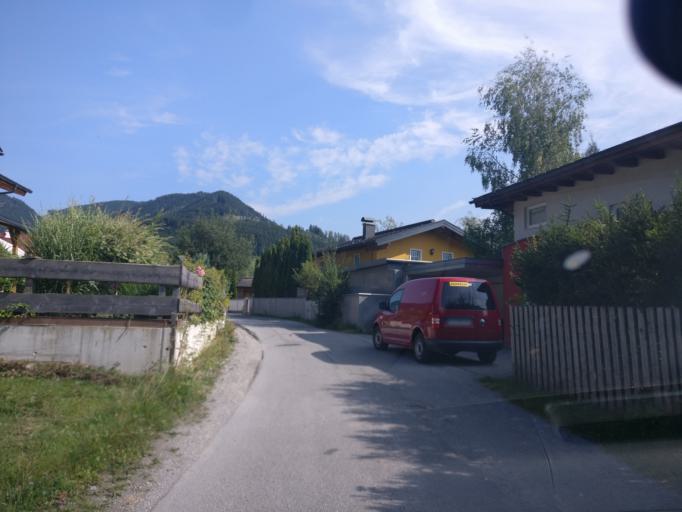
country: AT
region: Salzburg
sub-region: Politischer Bezirk Sankt Johann im Pongau
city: Werfenweng
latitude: 47.4624
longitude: 13.2457
